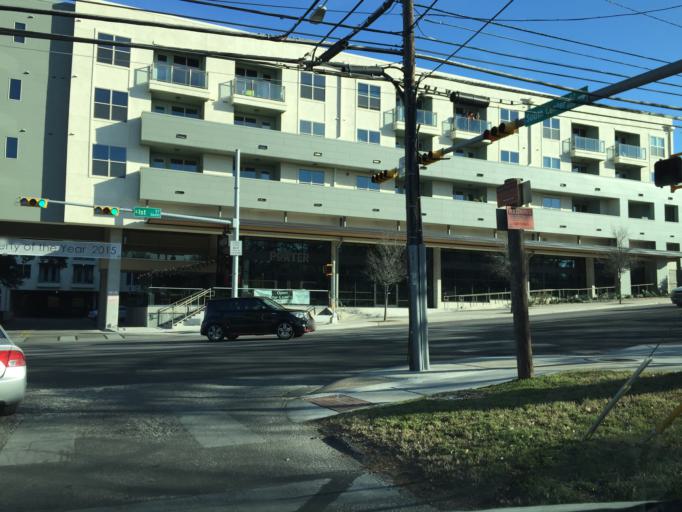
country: US
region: Texas
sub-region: Travis County
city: Austin
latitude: 30.2295
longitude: -97.7678
